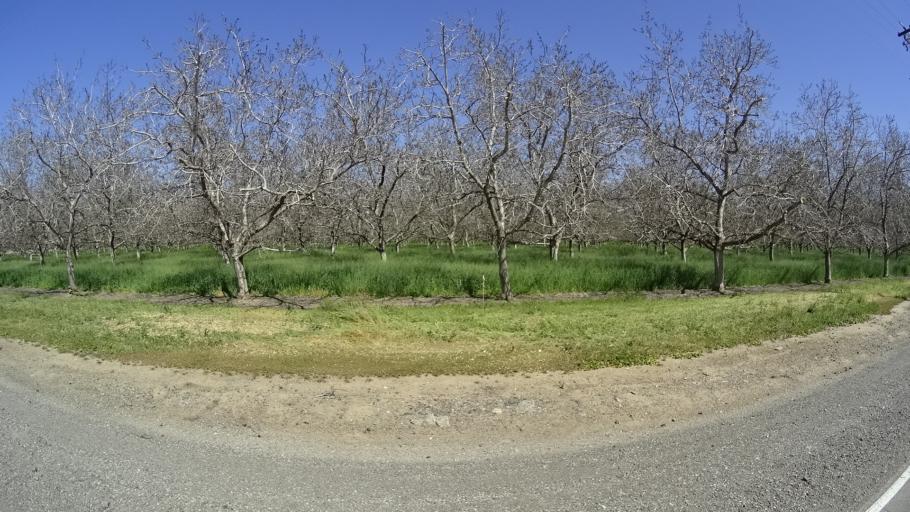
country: US
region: California
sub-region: Glenn County
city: Willows
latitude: 39.4644
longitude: -121.9888
